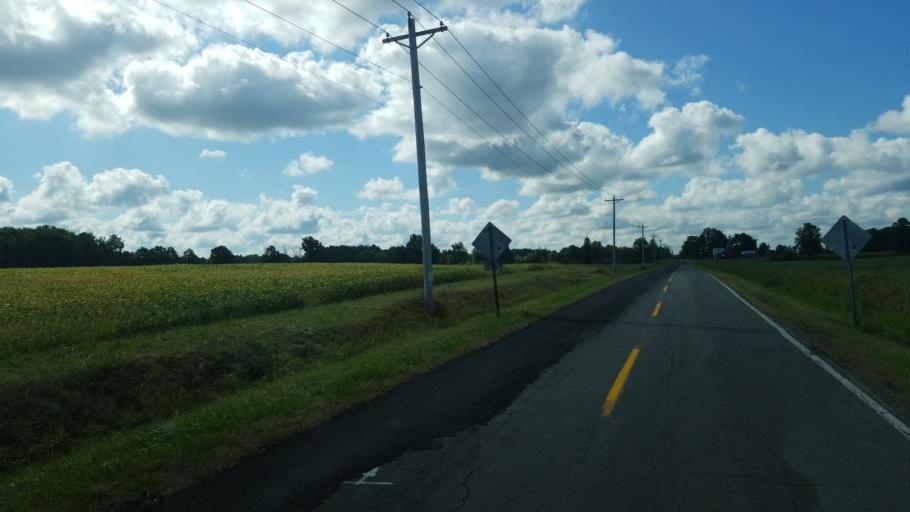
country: US
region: Ohio
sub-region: Lorain County
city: Lagrange
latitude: 41.2358
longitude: -82.1804
